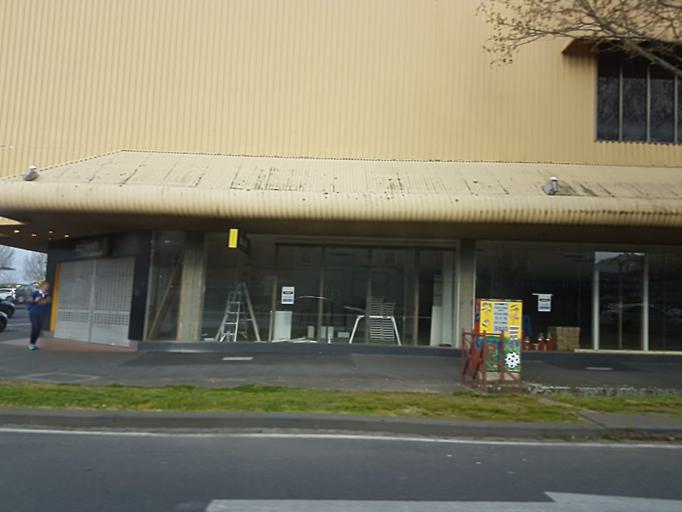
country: AU
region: Victoria
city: Ballarat East
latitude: -37.5618
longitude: 143.8608
